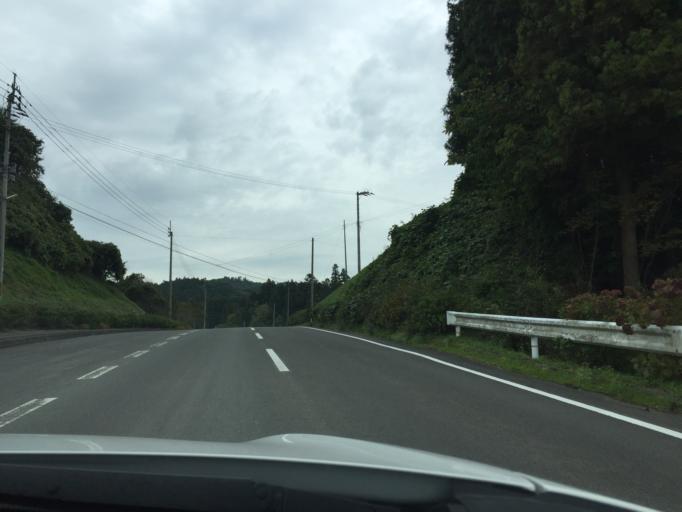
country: JP
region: Fukushima
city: Nihommatsu
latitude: 37.5830
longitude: 140.5599
